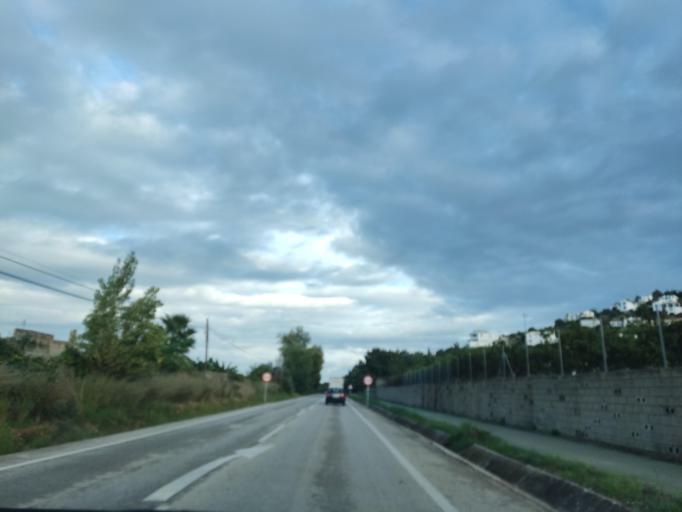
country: ES
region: Valencia
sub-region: Provincia de Alicante
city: Benimeli
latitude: 38.8518
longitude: -0.0547
